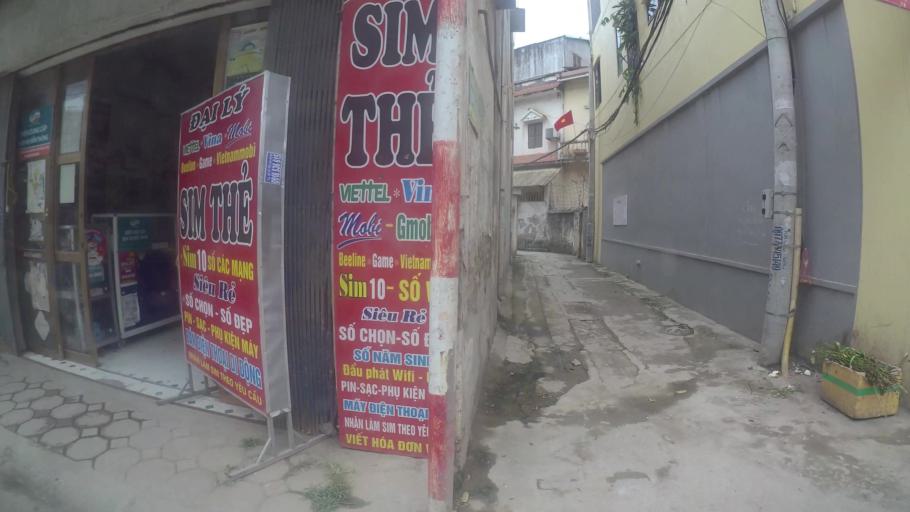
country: VN
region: Ha Noi
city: Tay Ho
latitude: 21.0794
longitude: 105.7858
